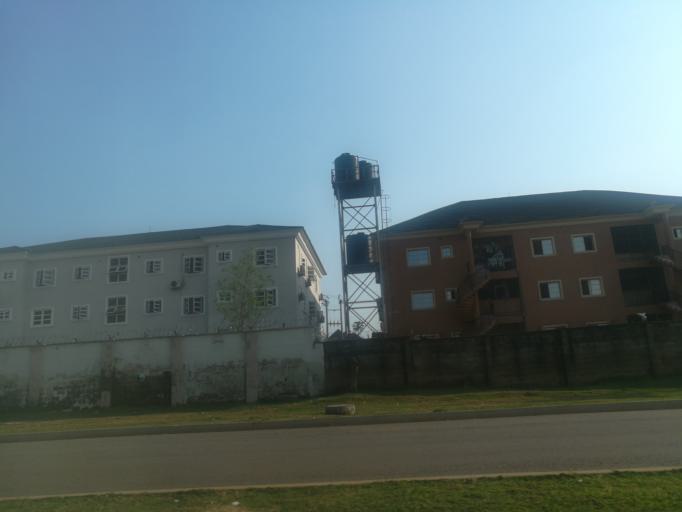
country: NG
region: Abuja Federal Capital Territory
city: Abuja
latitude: 9.0455
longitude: 7.4407
